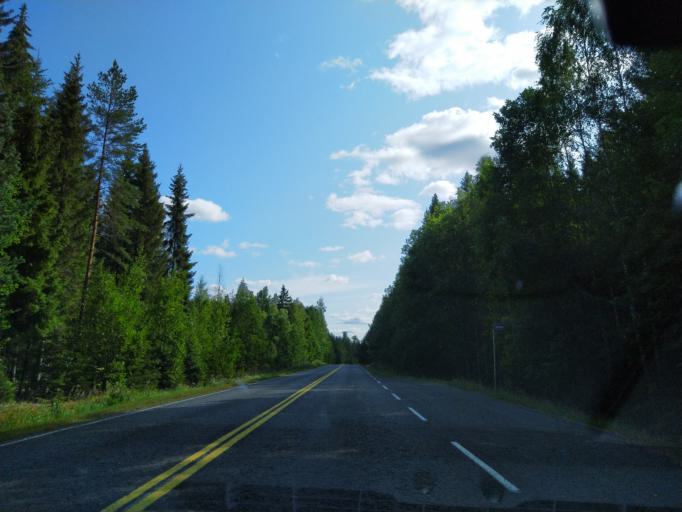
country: FI
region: Uusimaa
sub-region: Helsinki
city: Karkkila
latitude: 60.5826
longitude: 24.2312
